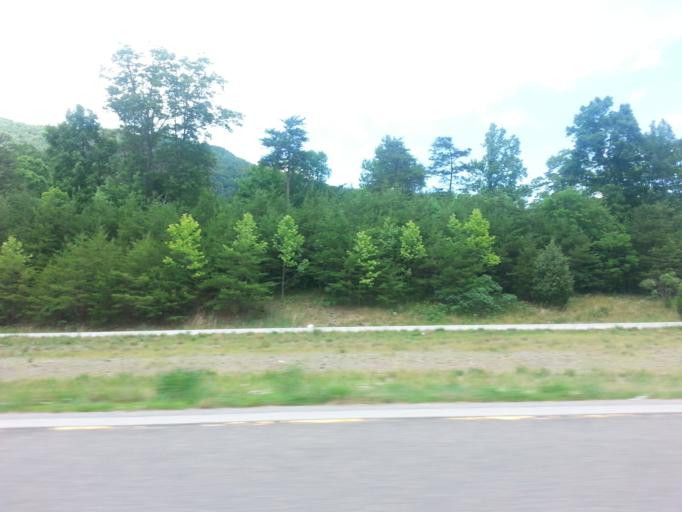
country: US
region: Tennessee
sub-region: Claiborne County
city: Harrogate
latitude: 36.6023
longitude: -83.6510
